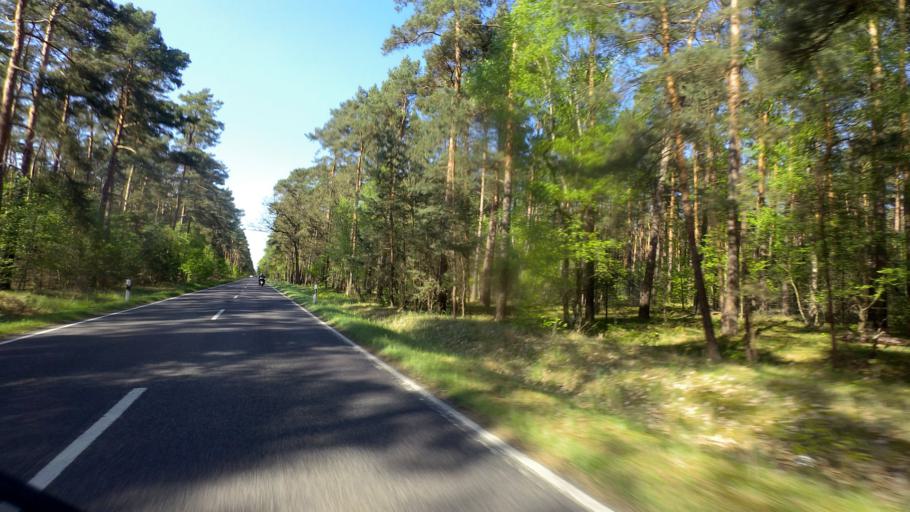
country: DE
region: Brandenburg
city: Gross Koris
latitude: 52.2012
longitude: 13.6935
